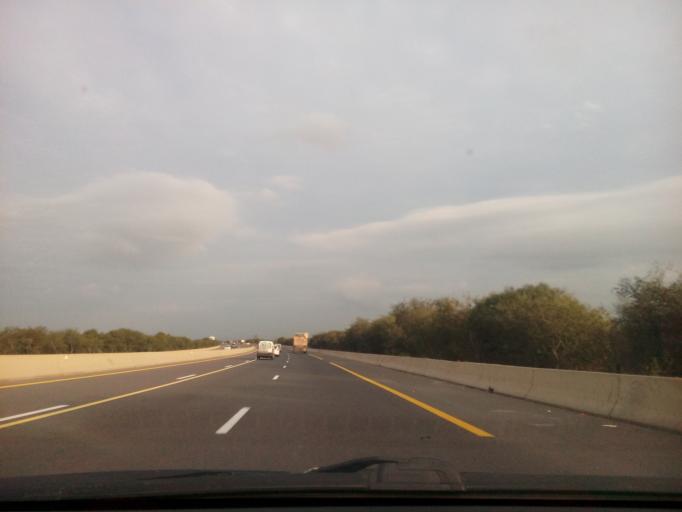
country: DZ
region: Relizane
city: Relizane
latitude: 35.7887
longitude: 0.4147
